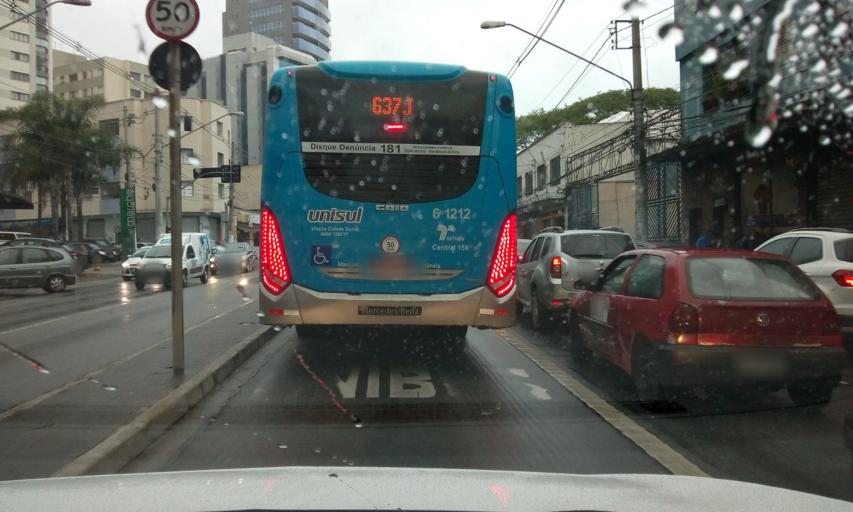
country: BR
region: Sao Paulo
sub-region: Sao Paulo
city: Sao Paulo
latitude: -23.6013
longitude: -46.6741
